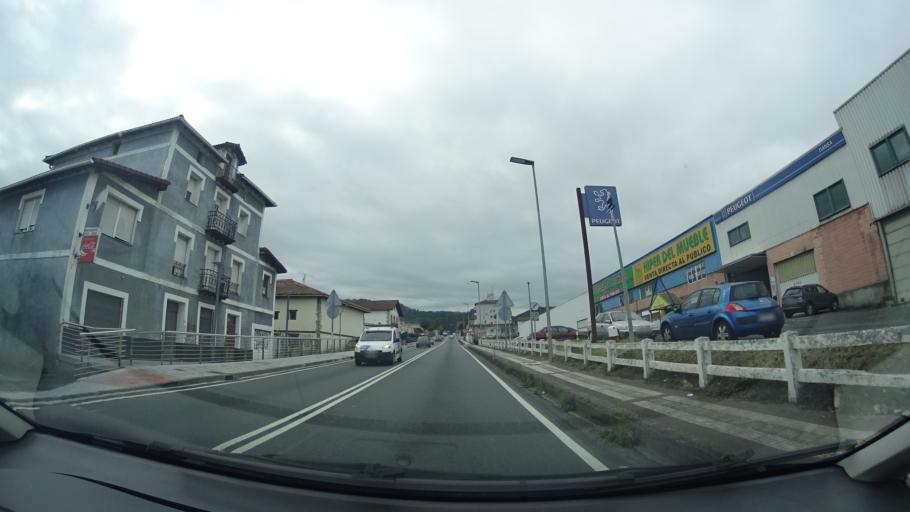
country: ES
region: Basque Country
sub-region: Bizkaia
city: Galdakao
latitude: 43.2163
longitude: -2.8129
